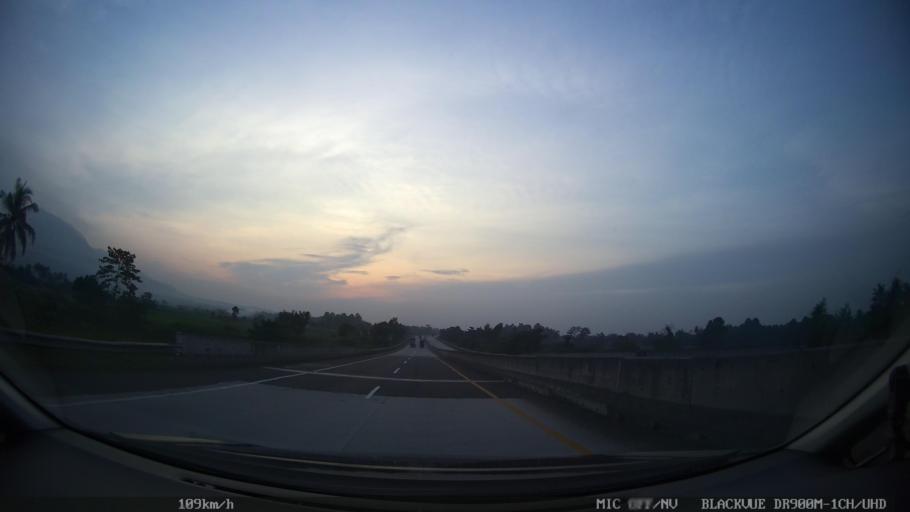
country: ID
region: Lampung
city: Pasuruan
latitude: -5.7323
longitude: 105.6825
